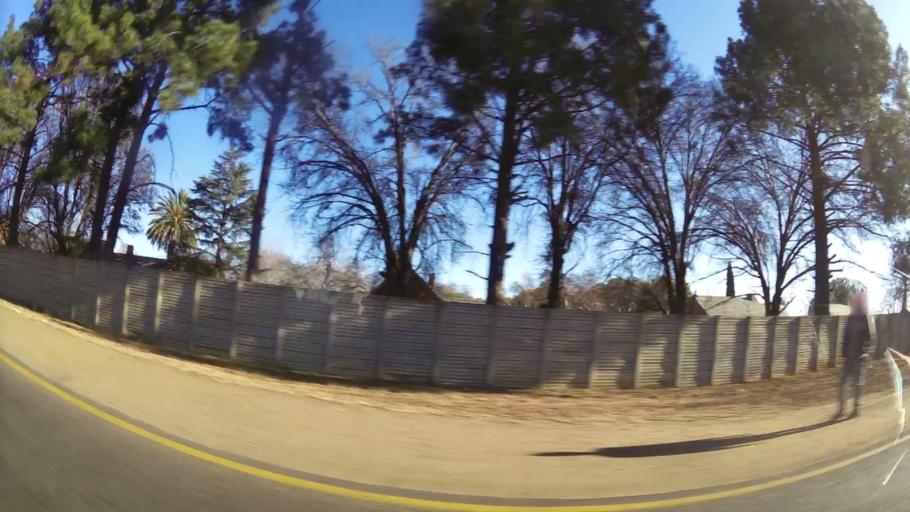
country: ZA
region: Gauteng
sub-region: Ekurhuleni Metropolitan Municipality
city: Tembisa
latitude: -26.0399
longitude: 28.2492
